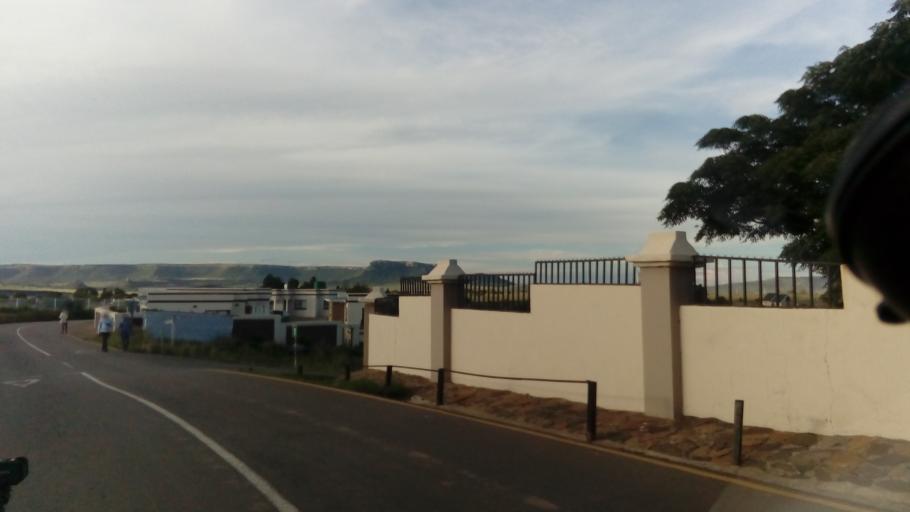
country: LS
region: Maseru
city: Maseru
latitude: -29.3094
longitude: 27.5014
